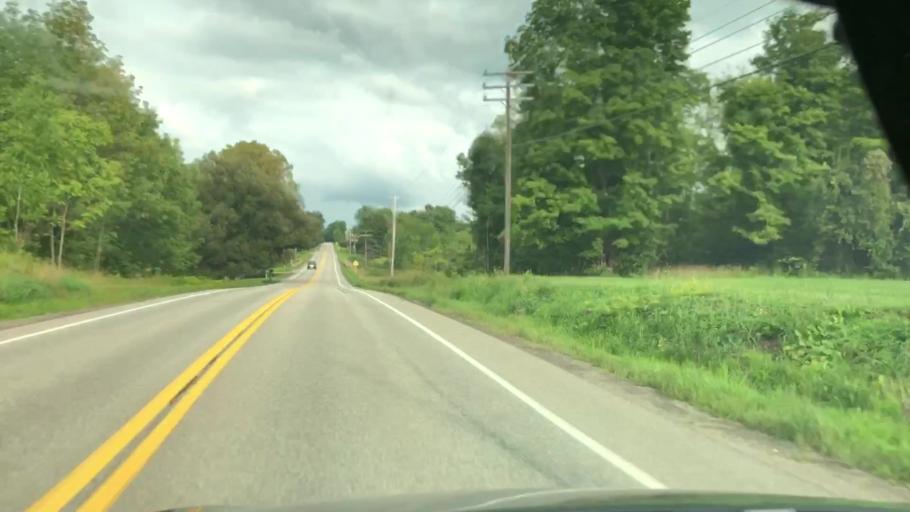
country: US
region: Pennsylvania
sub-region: Erie County
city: Northwest Harborcreek
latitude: 42.0575
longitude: -79.9112
